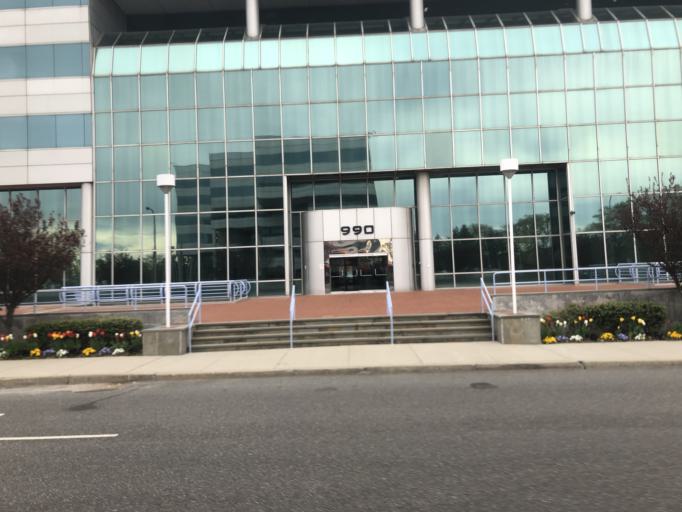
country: US
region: New York
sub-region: Nassau County
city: East Garden City
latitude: 40.7340
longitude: -73.5973
